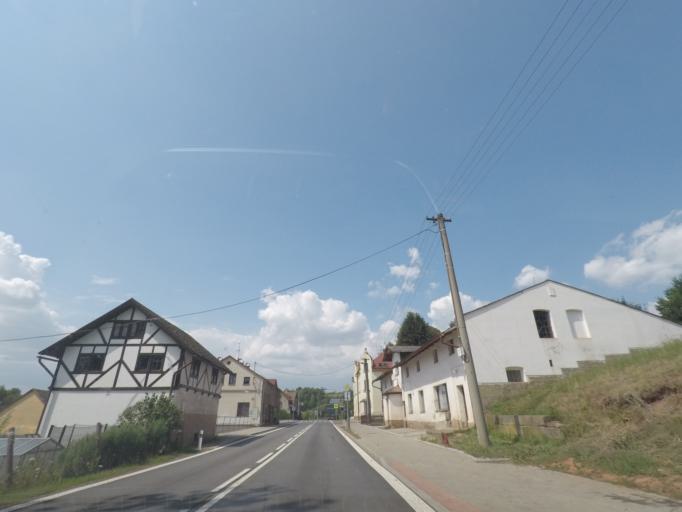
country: CZ
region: Kralovehradecky
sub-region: Okres Trutnov
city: Hostinne
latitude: 50.5212
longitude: 15.7673
